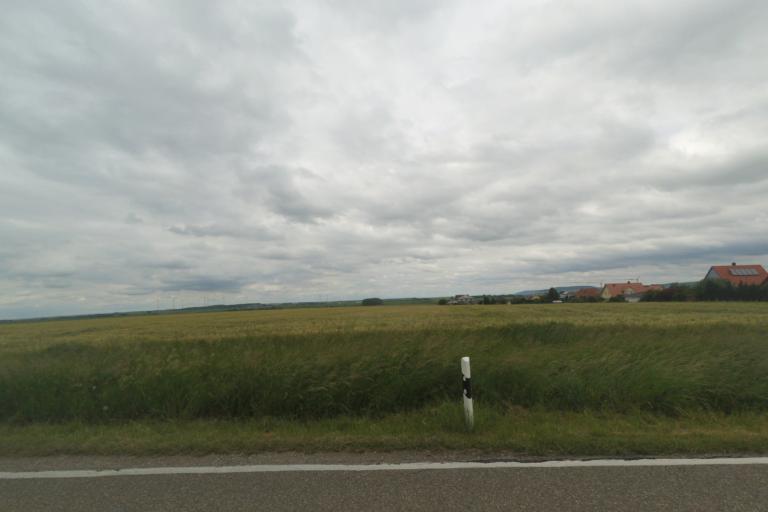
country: DE
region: Bavaria
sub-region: Regierungsbezirk Mittelfranken
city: Uffenheim
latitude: 49.5431
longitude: 10.2127
